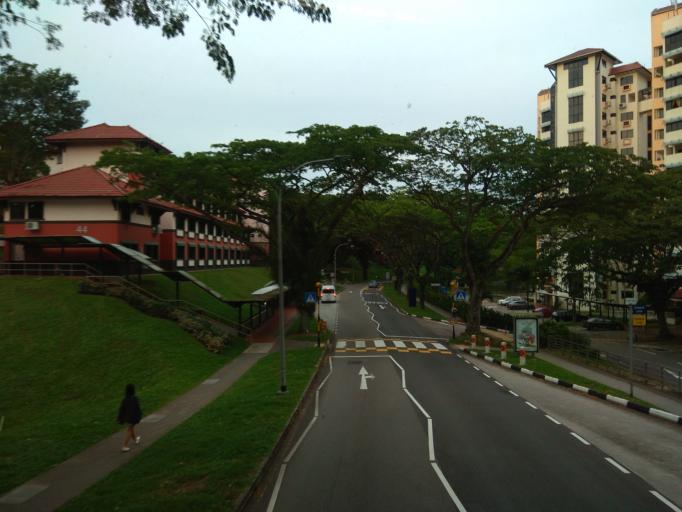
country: MY
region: Johor
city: Johor Bahru
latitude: 1.3509
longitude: 103.6858
